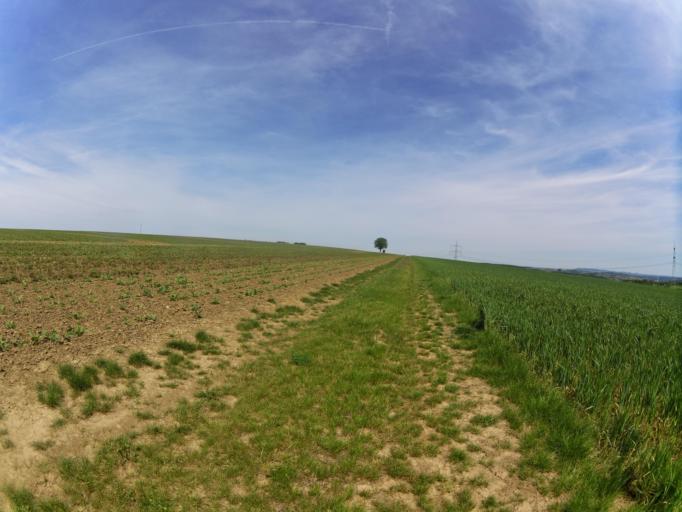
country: DE
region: Bavaria
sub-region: Regierungsbezirk Unterfranken
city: Ochsenfurt
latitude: 49.6629
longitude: 10.0294
